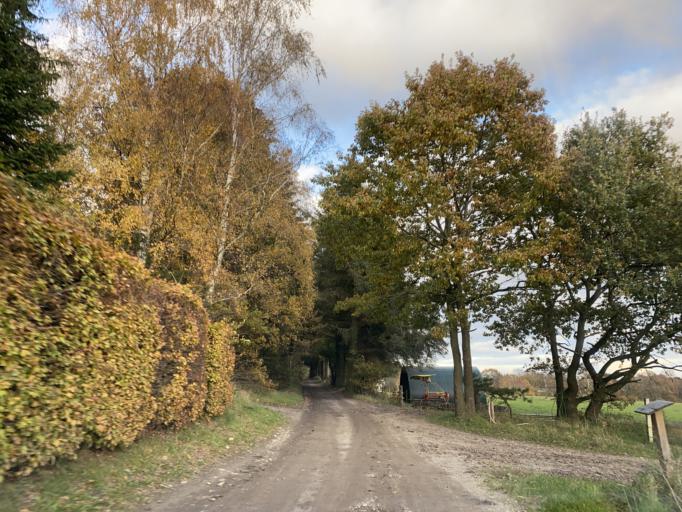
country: DK
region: Central Jutland
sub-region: Silkeborg Kommune
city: Svejbaek
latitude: 56.1780
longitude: 9.6008
